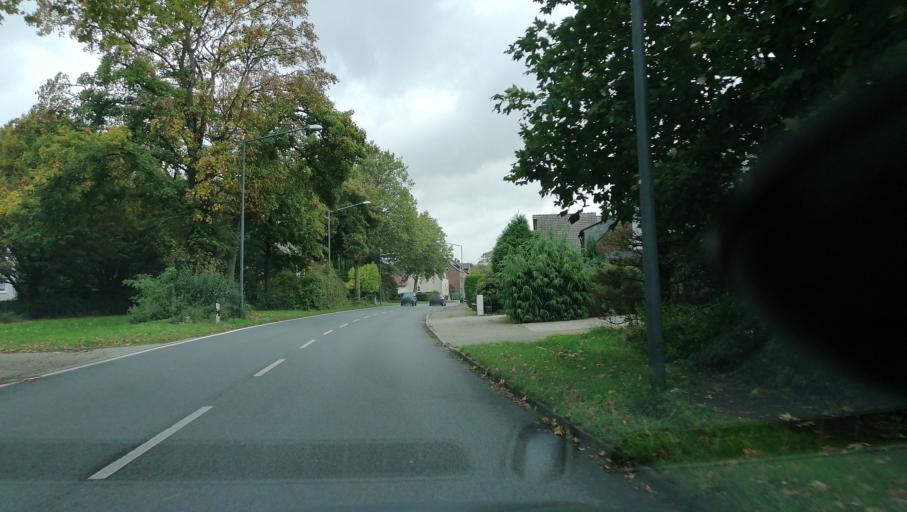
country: DE
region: North Rhine-Westphalia
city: Herten
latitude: 51.6150
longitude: 7.1481
